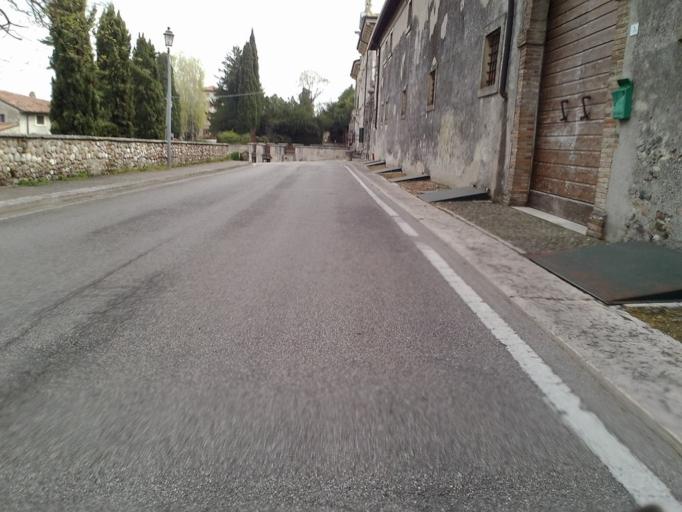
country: IT
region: Veneto
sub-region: Provincia di Verona
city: Rosegaferro
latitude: 45.3732
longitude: 10.7956
